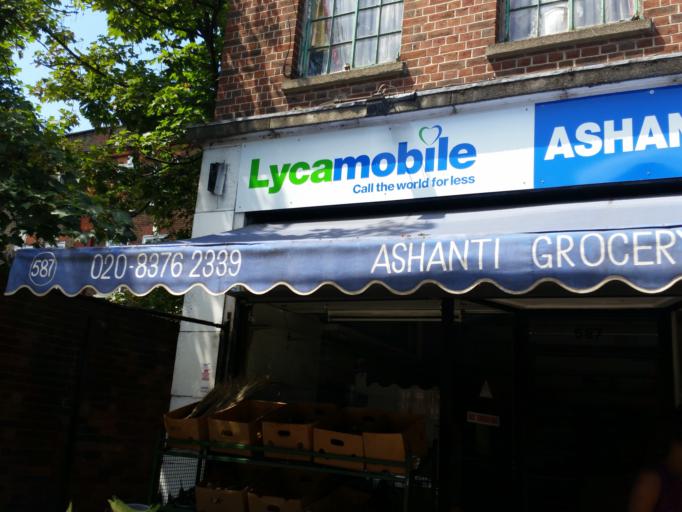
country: GB
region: England
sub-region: Greater London
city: Harringay
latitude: 51.5966
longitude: -0.0686
